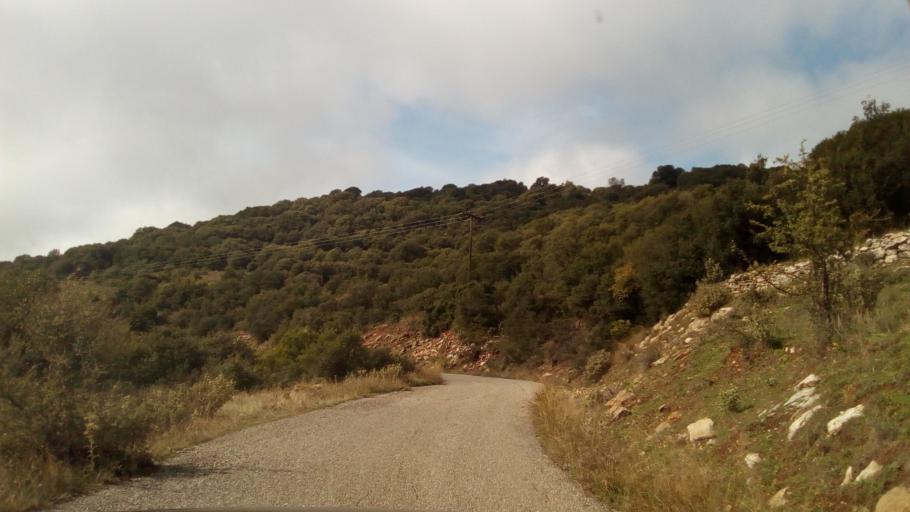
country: GR
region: West Greece
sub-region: Nomos Achaias
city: Kamarai
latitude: 38.4559
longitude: 21.9815
